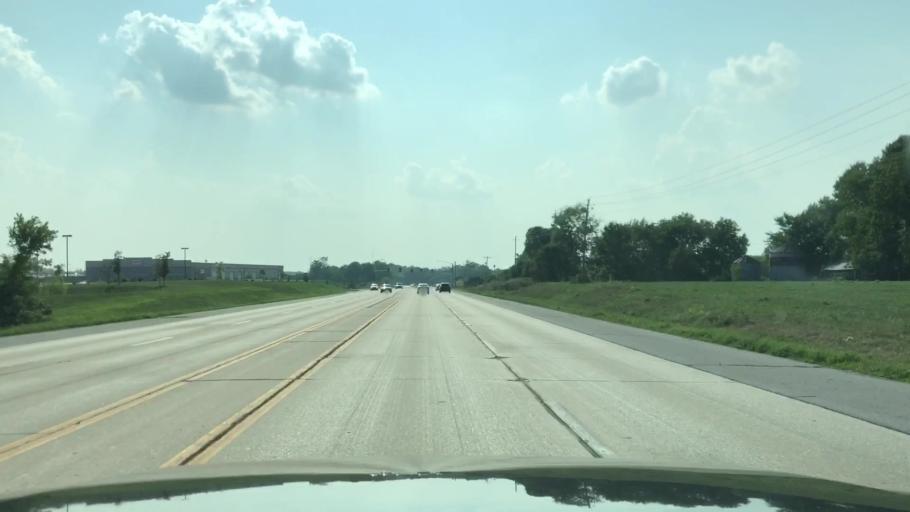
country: US
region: Missouri
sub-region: Saint Charles County
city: Wentzville
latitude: 38.8271
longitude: -90.8370
